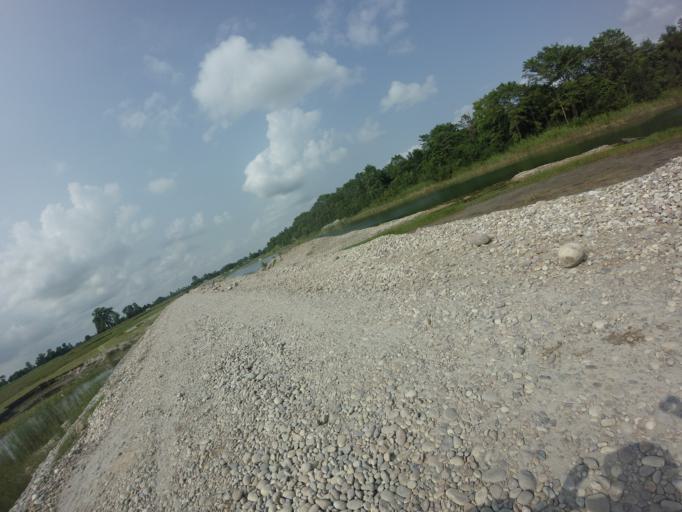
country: NP
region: Far Western
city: Tikapur
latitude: 28.4471
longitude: 81.0749
